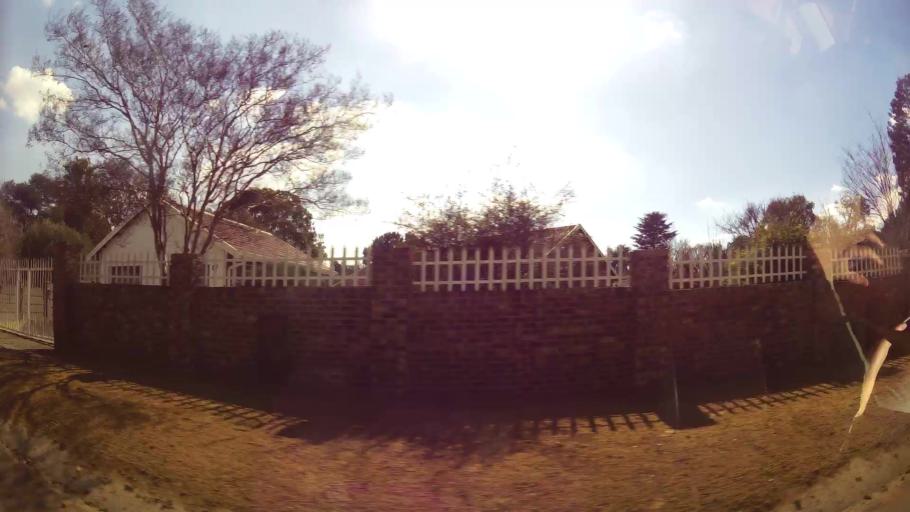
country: ZA
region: Mpumalanga
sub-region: Nkangala District Municipality
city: Witbank
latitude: -25.9471
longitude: 29.2478
